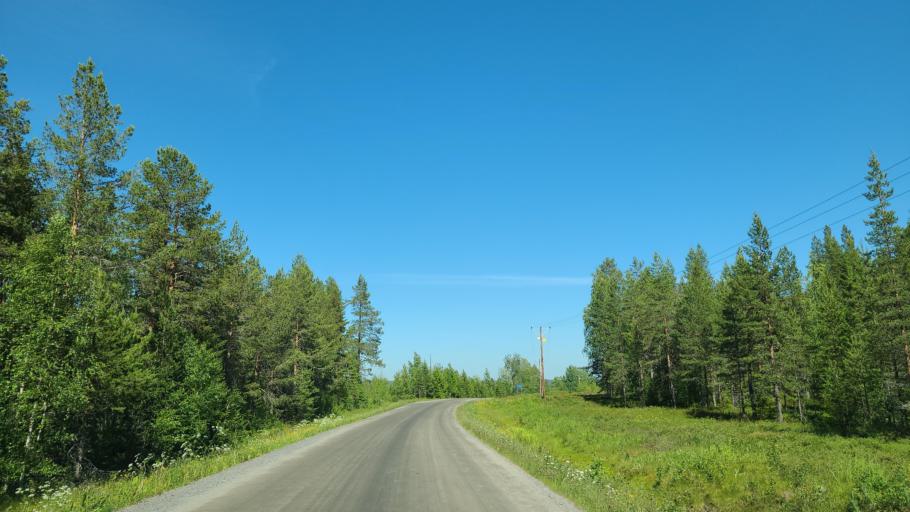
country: SE
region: Vaesterbotten
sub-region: Bjurholms Kommun
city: Bjurholm
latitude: 63.6437
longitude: 19.2145
